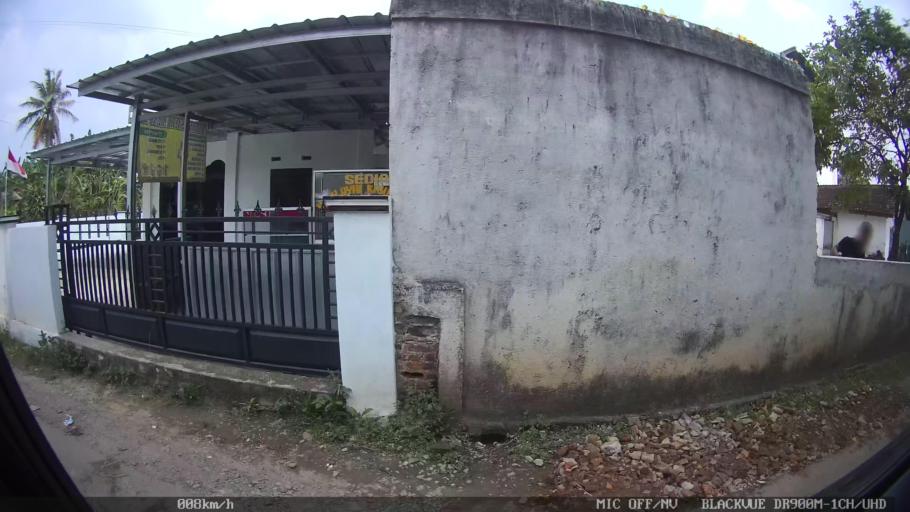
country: ID
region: Lampung
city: Gadingrejo
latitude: -5.3694
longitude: 105.0569
